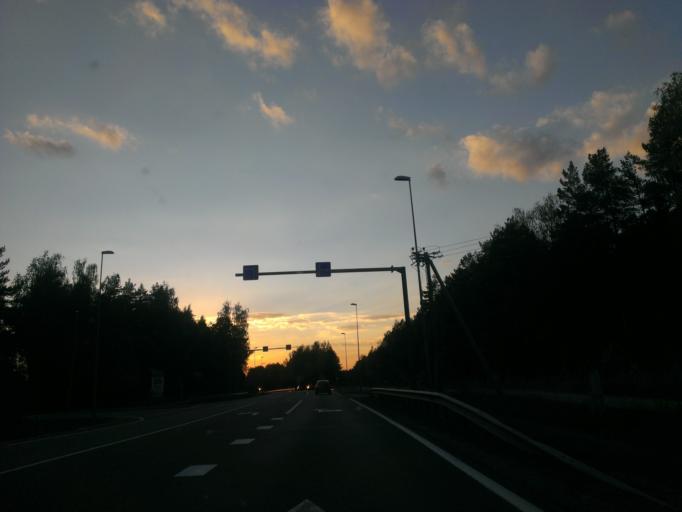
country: LV
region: Sigulda
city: Sigulda
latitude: 57.1344
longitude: 24.7838
